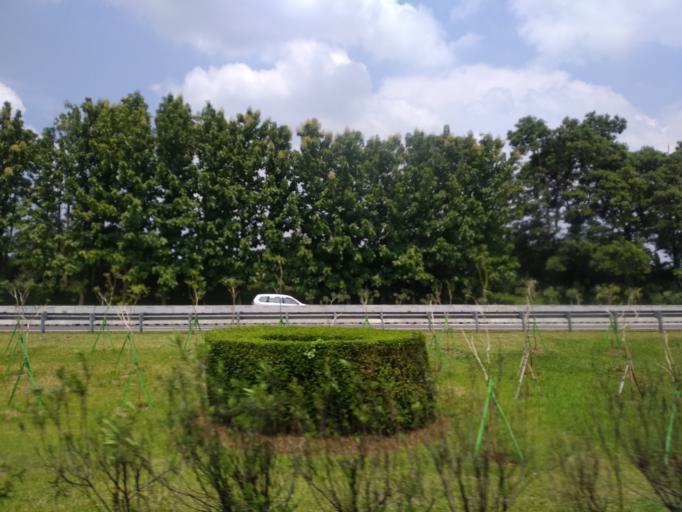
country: ID
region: West Java
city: Bogor
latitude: -6.5962
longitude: 106.8288
